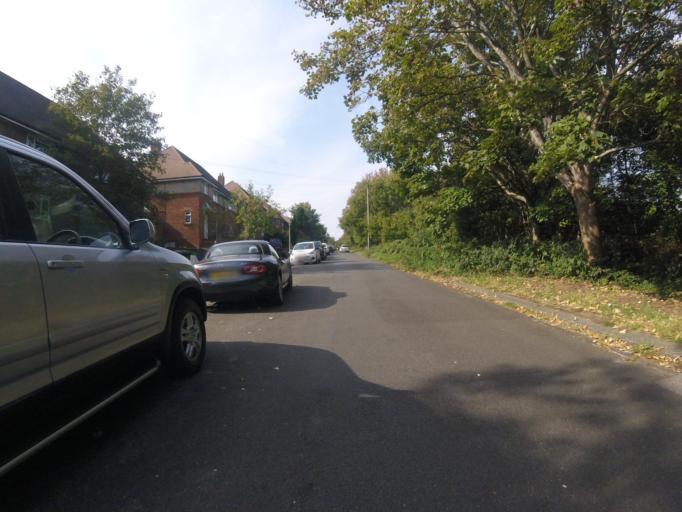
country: GB
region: England
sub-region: Brighton and Hove
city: Hove
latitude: 50.8509
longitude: -0.1861
